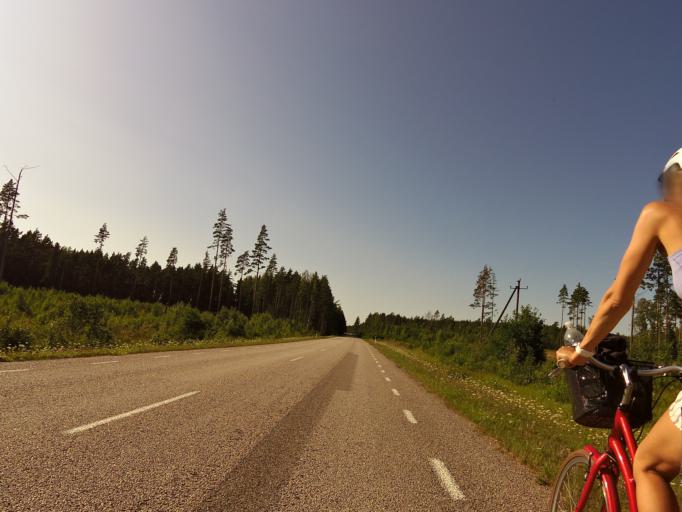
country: EE
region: Hiiumaa
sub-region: Kaerdla linn
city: Kardla
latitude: 58.8996
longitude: 22.4173
